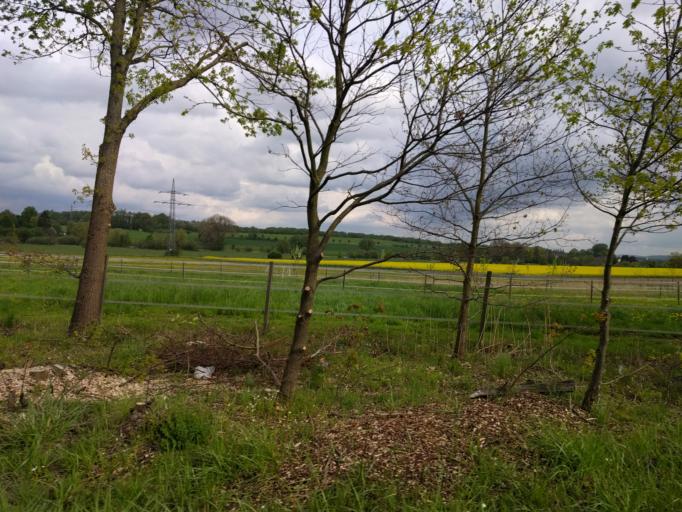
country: DE
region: North Rhine-Westphalia
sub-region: Regierungsbezirk Detmold
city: Bielefeld
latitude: 52.0518
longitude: 8.5767
